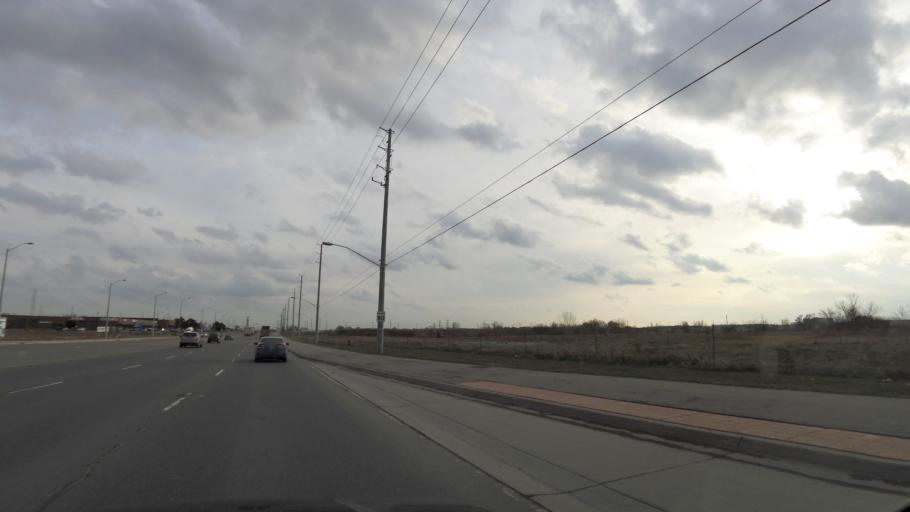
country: CA
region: Ontario
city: Brampton
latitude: 43.7732
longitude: -79.6522
